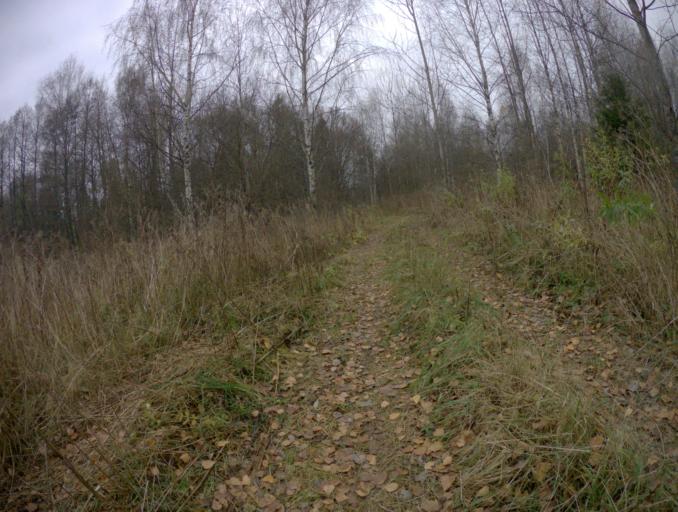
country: RU
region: Vladimir
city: Golovino
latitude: 56.0025
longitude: 40.5490
